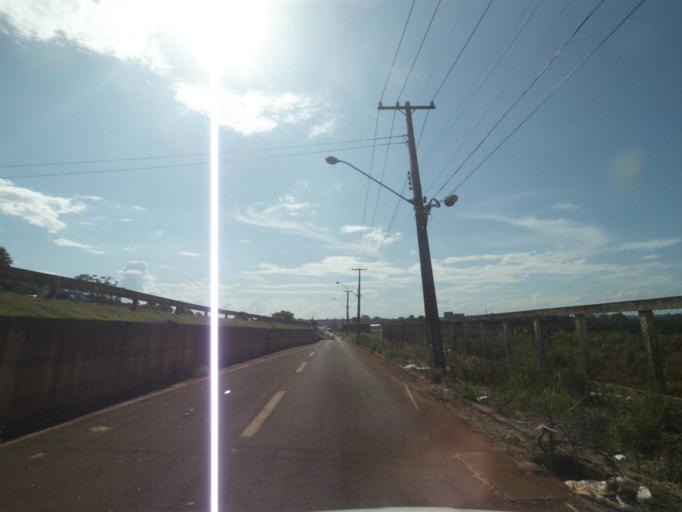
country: BR
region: Parana
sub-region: Londrina
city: Londrina
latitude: -23.3225
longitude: -51.1976
